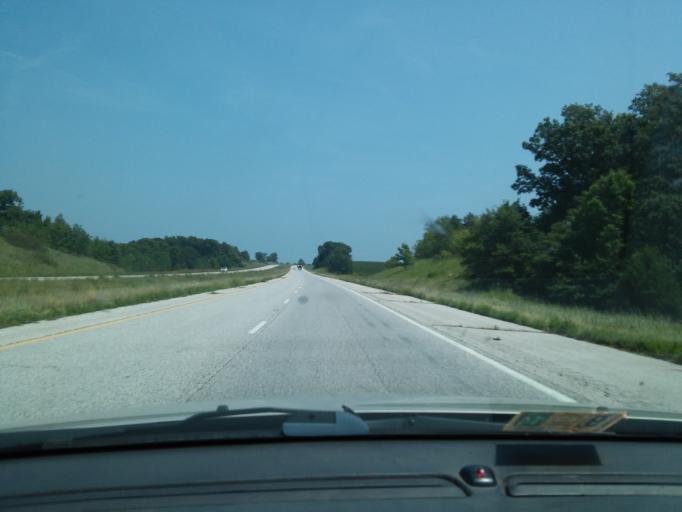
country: US
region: Illinois
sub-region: Pike County
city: Griggsville
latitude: 39.6751
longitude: -90.7389
